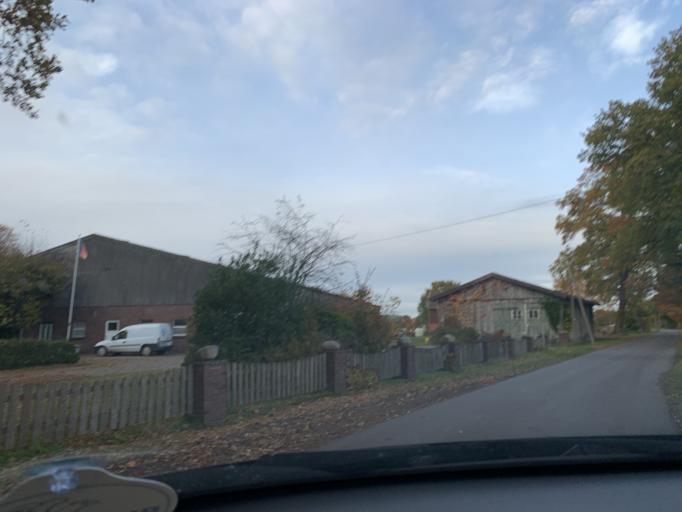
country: DE
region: Lower Saxony
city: Wiefelstede
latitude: 53.2553
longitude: 8.0869
